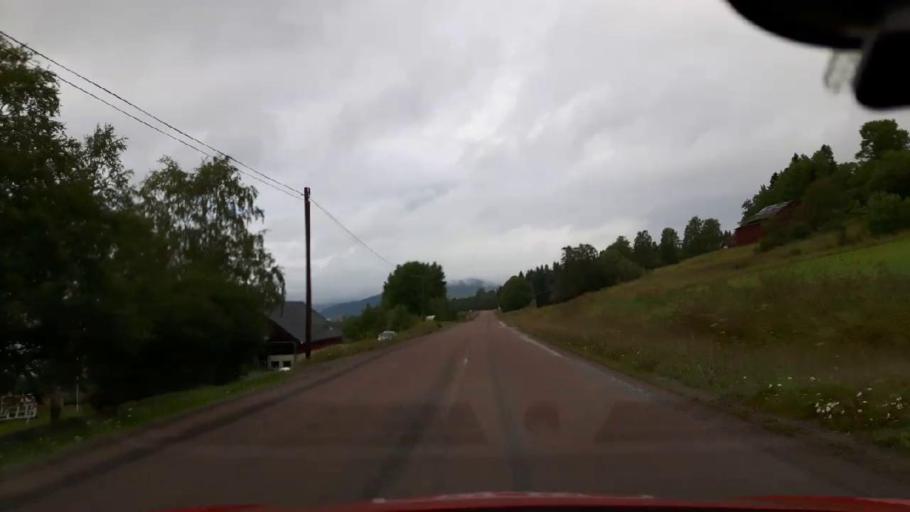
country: SE
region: Jaemtland
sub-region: Krokoms Kommun
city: Valla
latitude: 63.3611
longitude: 14.0674
